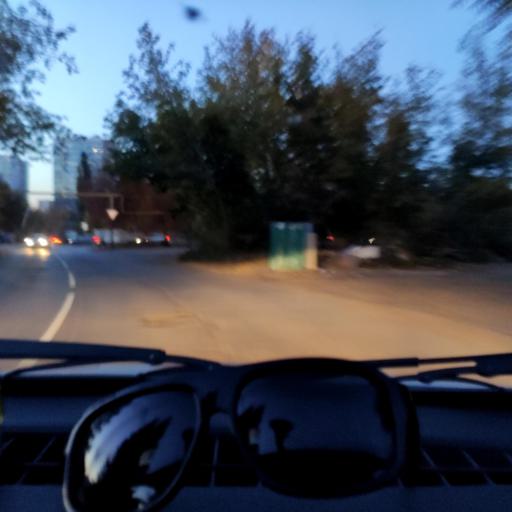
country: RU
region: Bashkortostan
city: Ufa
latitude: 54.7102
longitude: 55.9802
